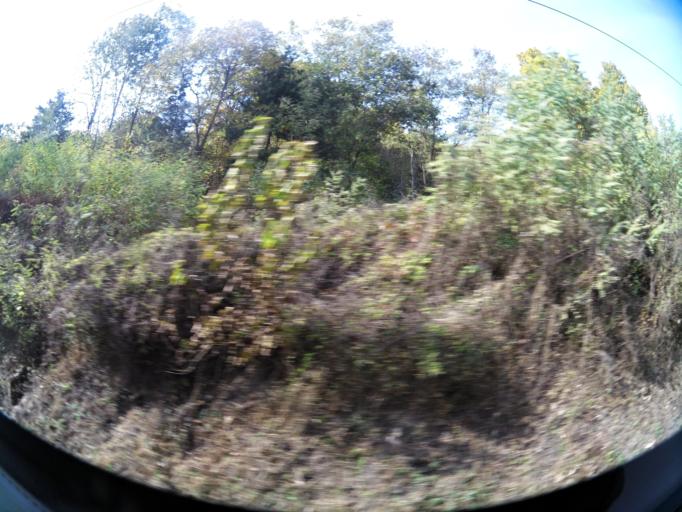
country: KR
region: Daejeon
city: Sintansin
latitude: 36.4715
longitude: 127.4213
